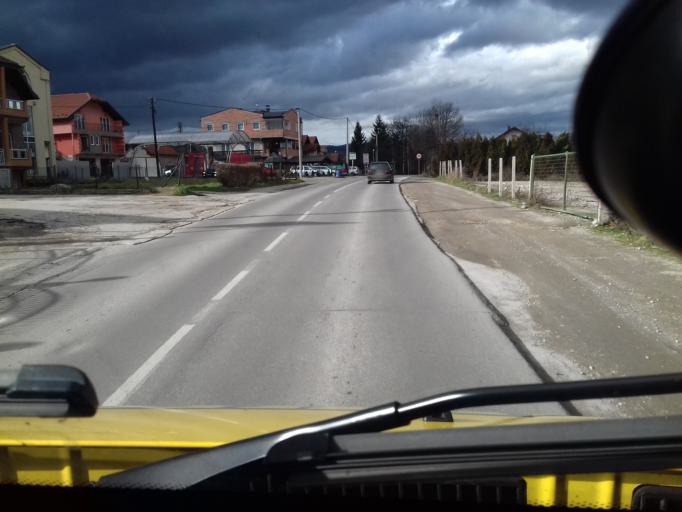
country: BA
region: Federation of Bosnia and Herzegovina
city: Gornje Mostre
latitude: 44.0102
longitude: 18.1462
